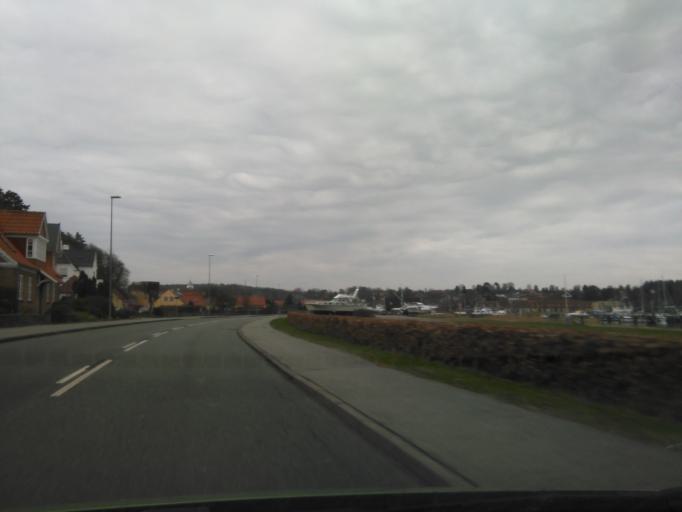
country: DK
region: North Denmark
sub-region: Mariagerfjord Kommune
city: Mariager
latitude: 56.6546
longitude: 9.9861
